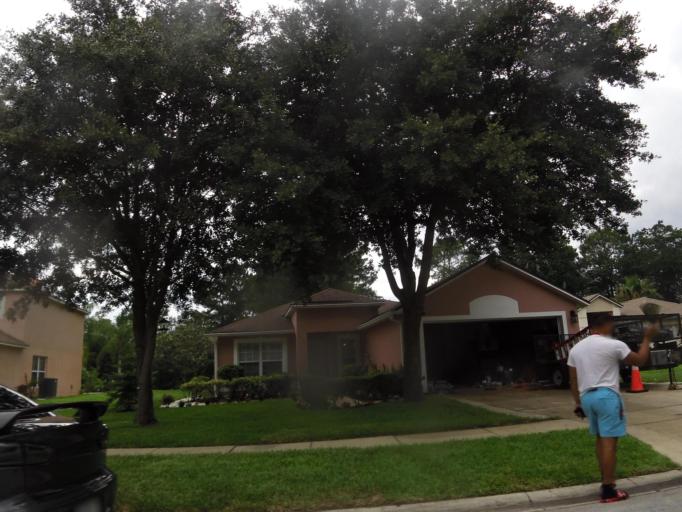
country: US
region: Florida
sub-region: Duval County
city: Jacksonville
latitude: 30.2991
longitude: -81.5421
